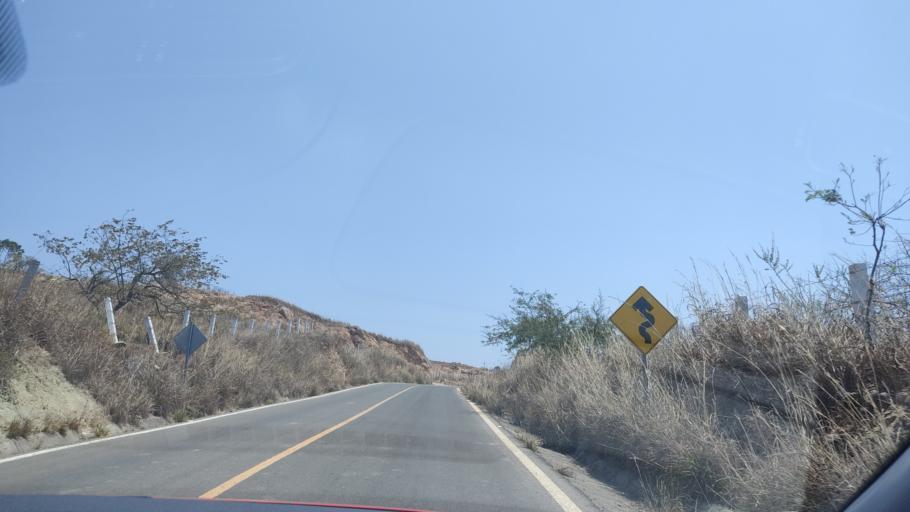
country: MX
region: Nayarit
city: Puga
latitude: 21.6106
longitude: -104.7347
